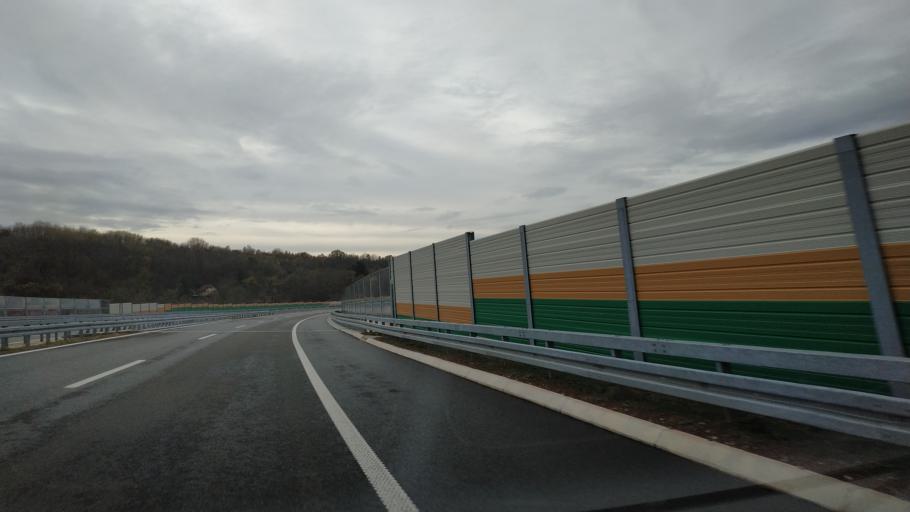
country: RS
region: Central Serbia
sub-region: Nisavski Okrug
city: Niska Banja
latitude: 43.3003
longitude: 22.0513
